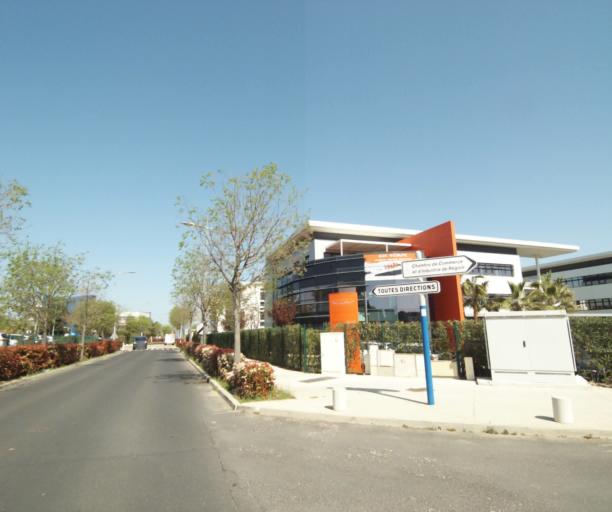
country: FR
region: Languedoc-Roussillon
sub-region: Departement de l'Herault
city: Perols
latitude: 43.5797
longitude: 3.9390
